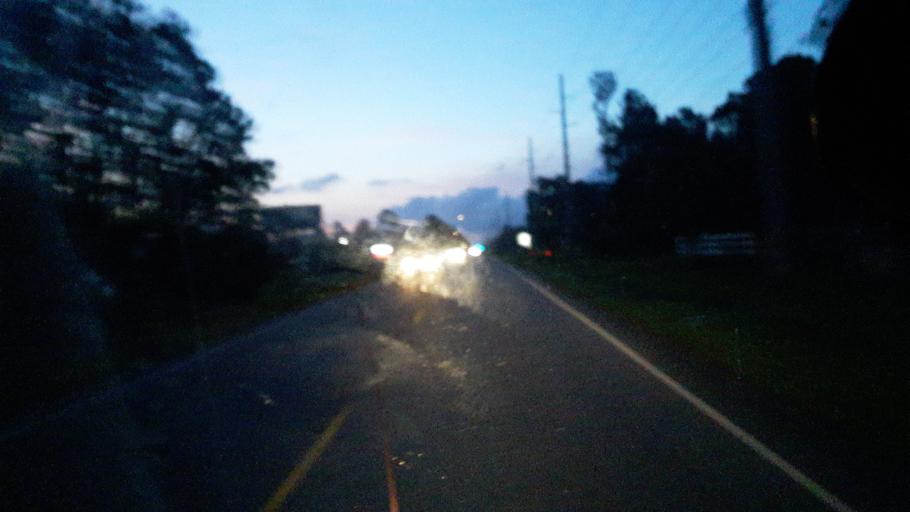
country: US
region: North Carolina
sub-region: Brunswick County
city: Oak Island
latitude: 33.9996
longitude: -78.2463
